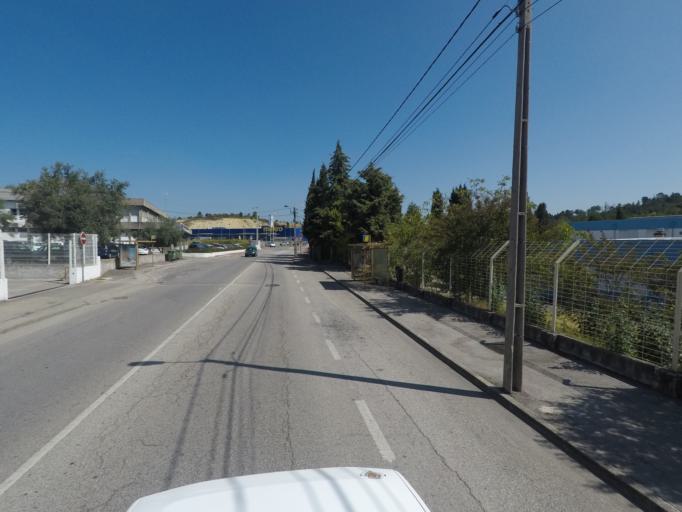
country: PT
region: Coimbra
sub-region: Coimbra
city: Coimbra
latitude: 40.2413
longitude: -8.4344
